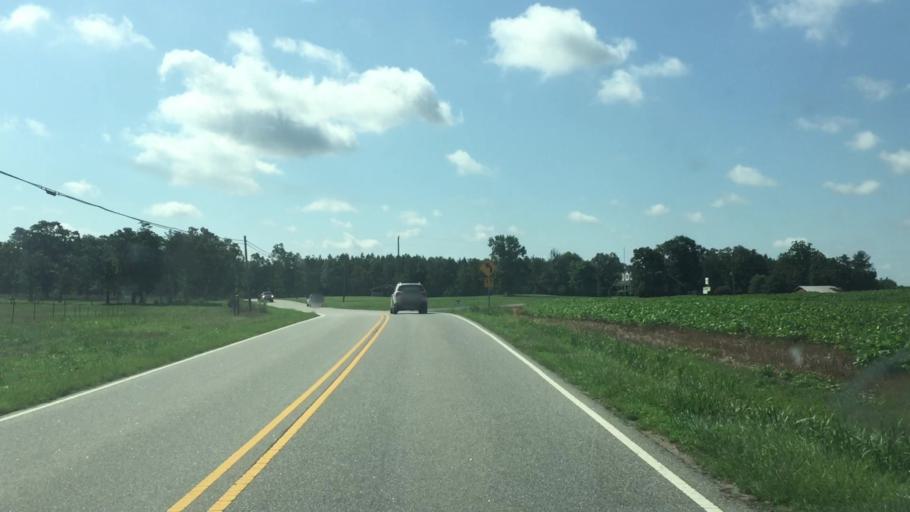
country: US
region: North Carolina
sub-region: Anson County
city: Polkton
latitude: 35.0335
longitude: -80.2440
